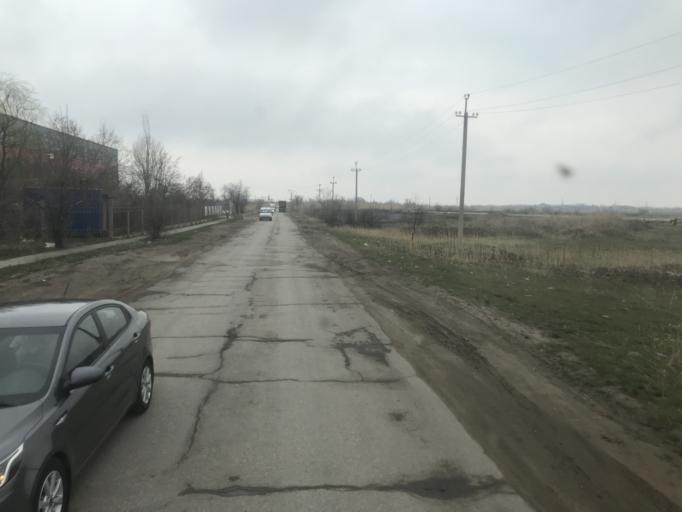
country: RU
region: Volgograd
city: Svetlyy Yar
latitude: 48.5262
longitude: 44.6145
